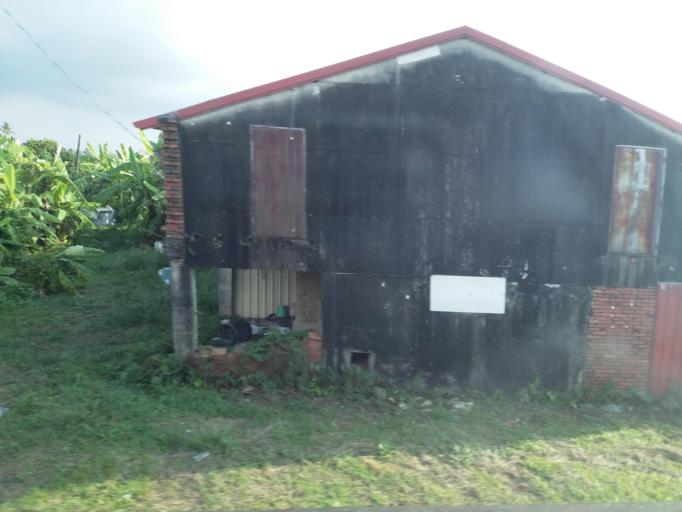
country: TW
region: Taiwan
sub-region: Pingtung
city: Pingtung
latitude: 22.8846
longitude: 120.5017
